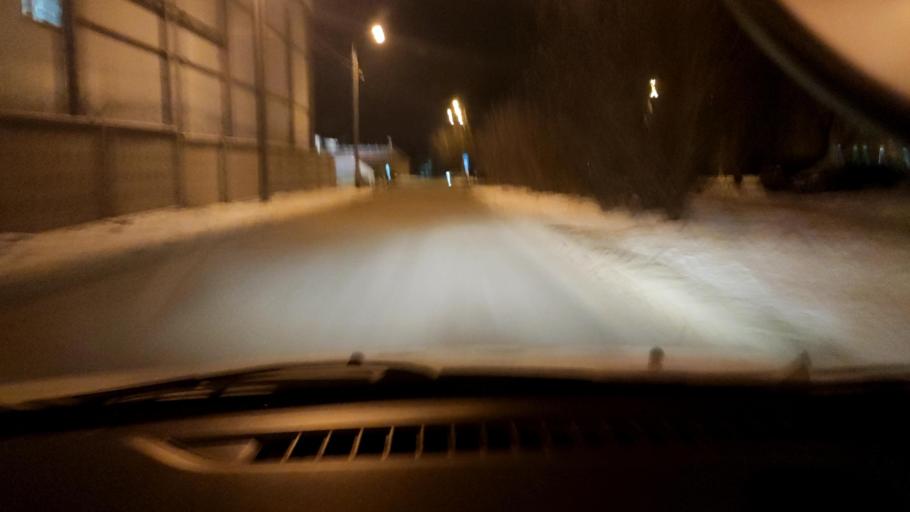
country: RU
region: Perm
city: Kondratovo
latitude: 58.0350
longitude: 56.0377
